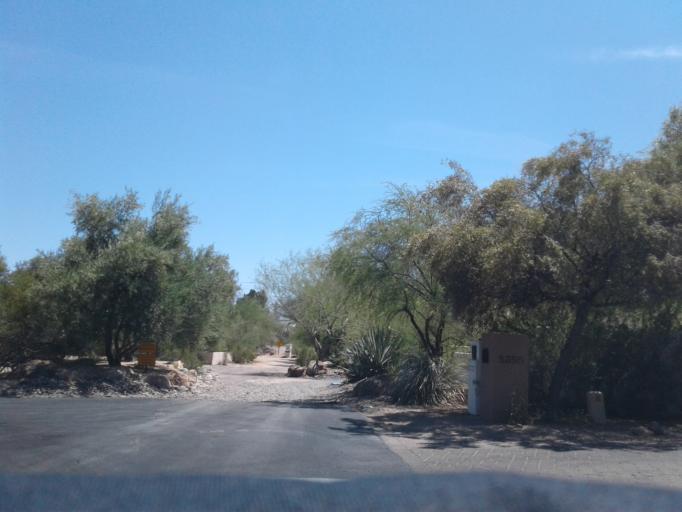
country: US
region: Arizona
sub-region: Maricopa County
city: Paradise Valley
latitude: 33.5161
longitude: -112.0041
